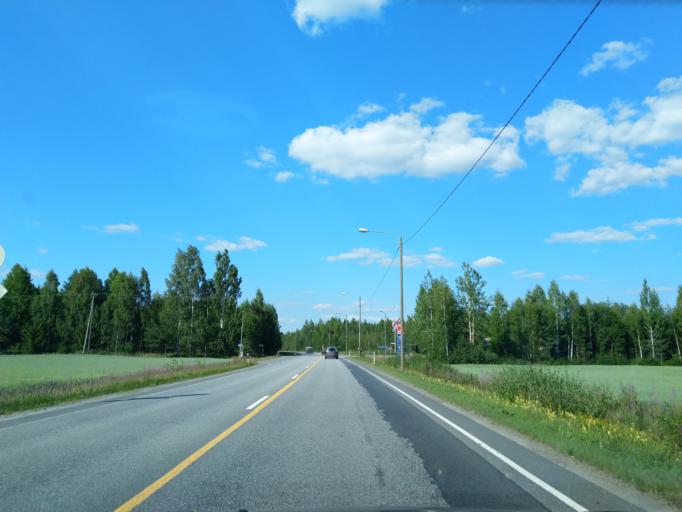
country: FI
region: Pirkanmaa
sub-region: Luoteis-Pirkanmaa
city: Kihnioe
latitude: 62.1747
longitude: 23.1686
